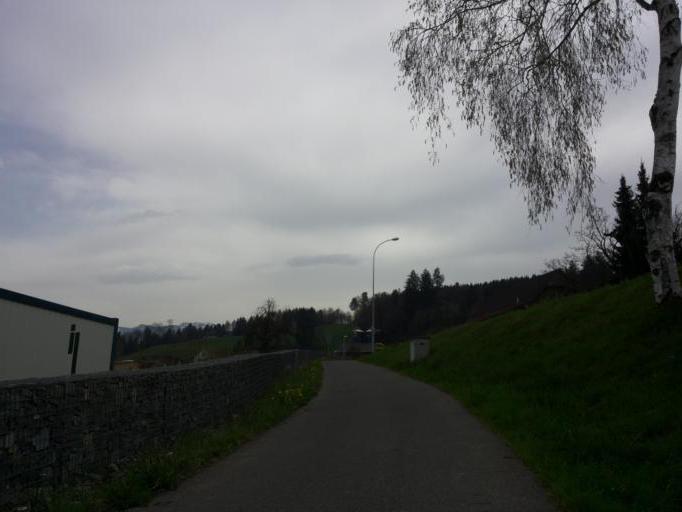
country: CH
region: Lucerne
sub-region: Lucerne-Land District
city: Meierskappel
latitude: 47.1395
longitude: 8.4574
